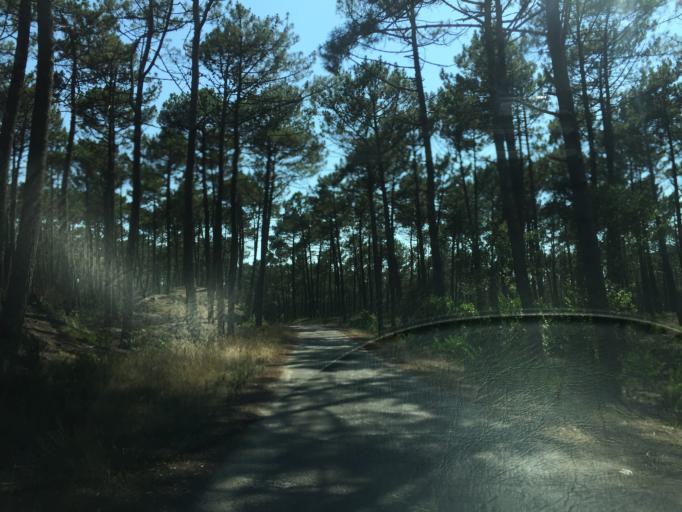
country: PT
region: Coimbra
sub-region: Figueira da Foz
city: Tavarede
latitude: 40.2519
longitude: -8.8409
